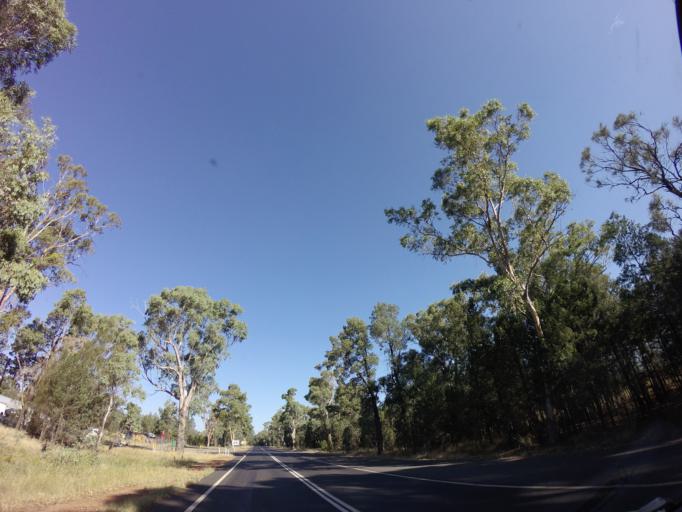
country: AU
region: New South Wales
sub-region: Gilgandra
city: Gilgandra
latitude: -31.7068
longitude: 148.6347
